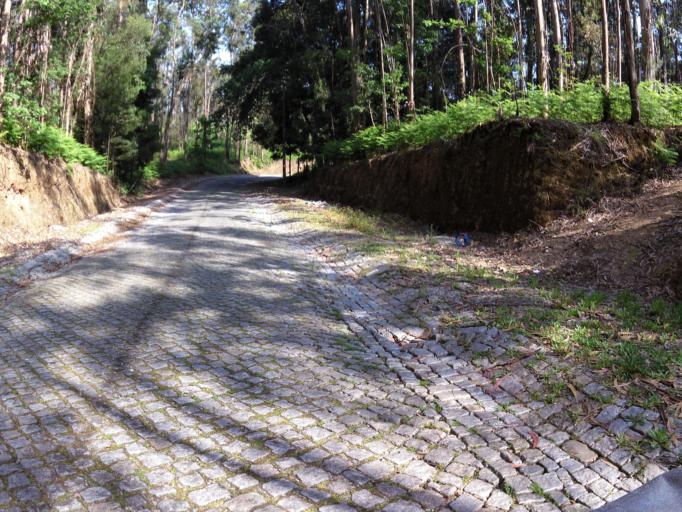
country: PT
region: Porto
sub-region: Vila Nova de Gaia
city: Olival
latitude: 41.0425
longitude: -8.5351
